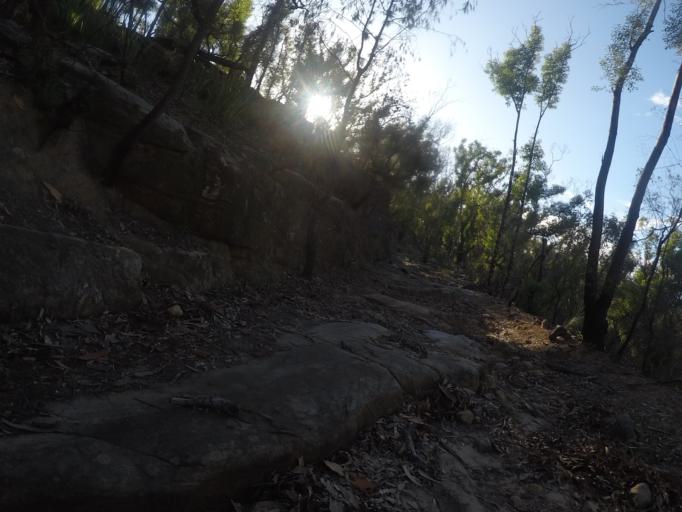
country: AU
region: New South Wales
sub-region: Hornsby Shire
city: Glenorie
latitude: -33.3494
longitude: 151.0102
